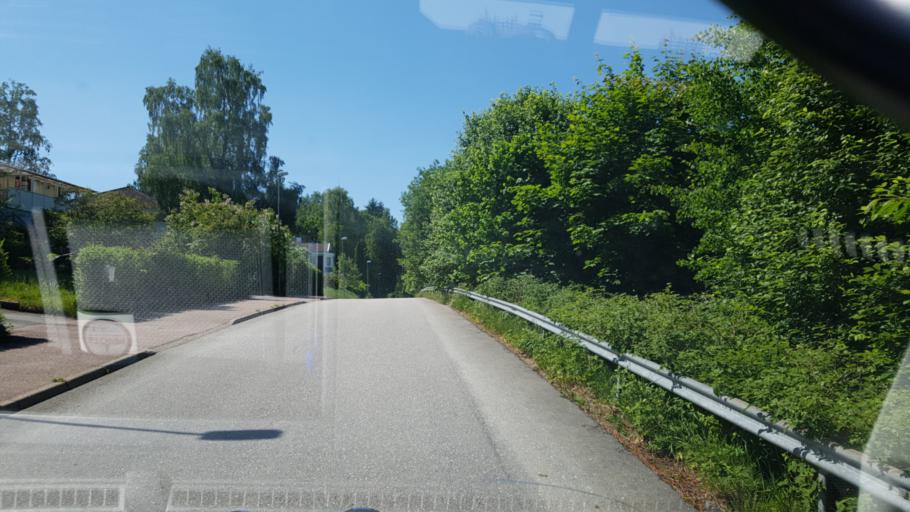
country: SE
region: Vaestra Goetaland
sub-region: Lerums Kommun
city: Stenkullen
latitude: 57.8039
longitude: 12.3570
